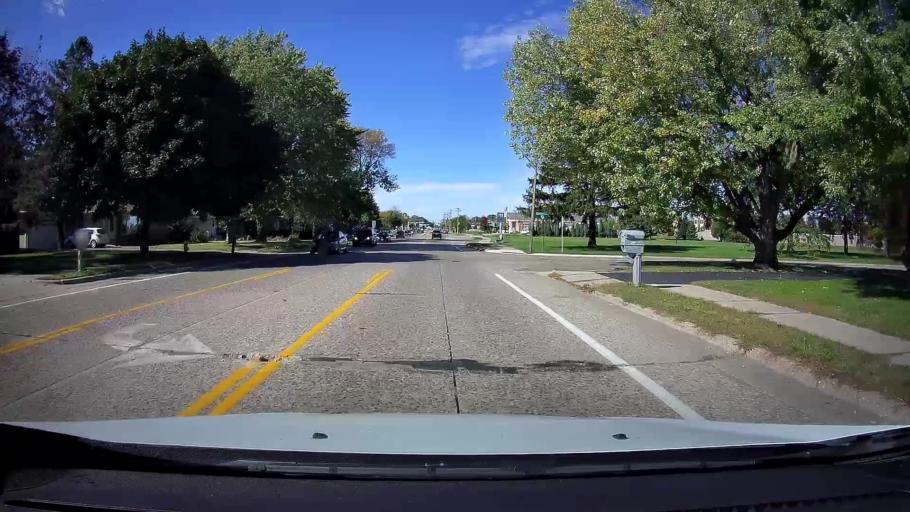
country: US
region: Minnesota
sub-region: Ramsey County
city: Roseville
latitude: 45.0063
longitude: -93.1588
